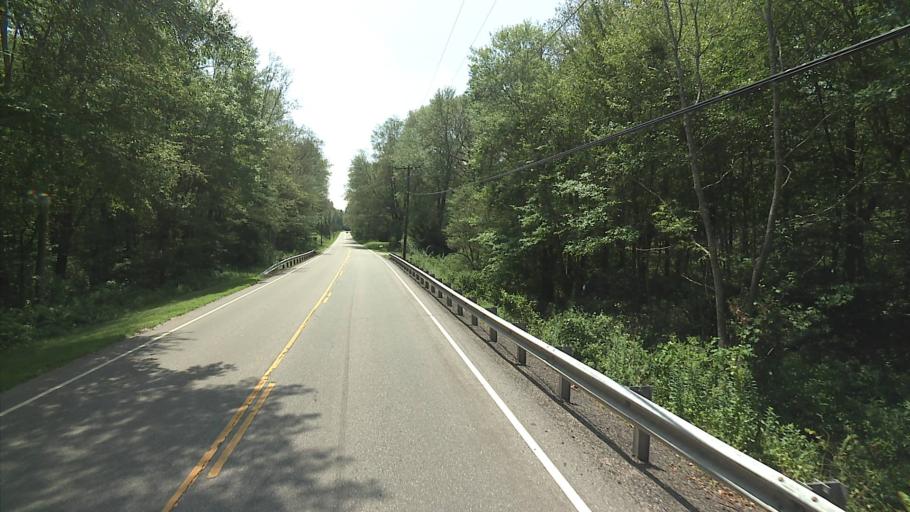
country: US
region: Connecticut
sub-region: New London County
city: Preston City
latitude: 41.5410
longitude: -71.9230
